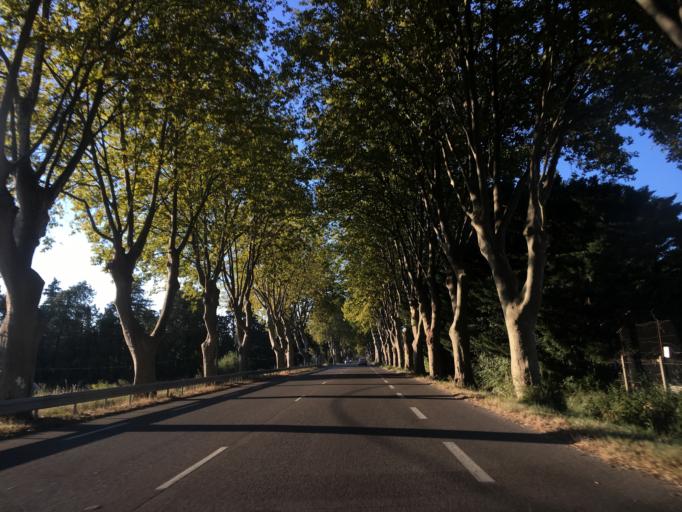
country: FR
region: Provence-Alpes-Cote d'Azur
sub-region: Departement des Bouches-du-Rhone
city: Orgon
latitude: 43.7808
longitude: 5.0510
